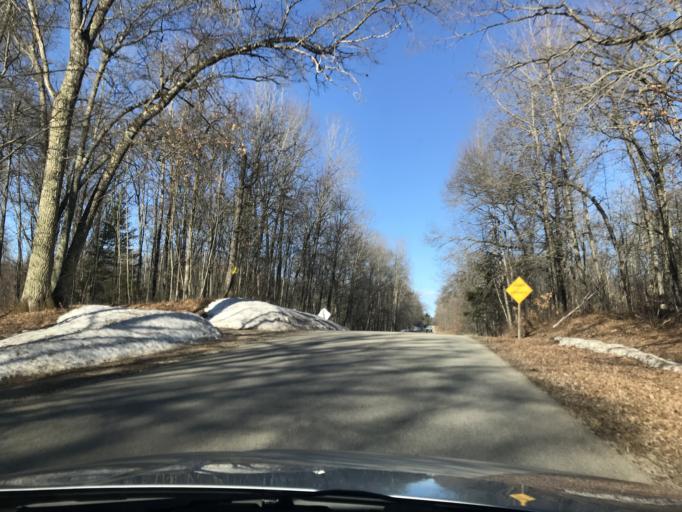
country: US
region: Wisconsin
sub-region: Marinette County
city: Niagara
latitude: 45.3903
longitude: -88.0699
